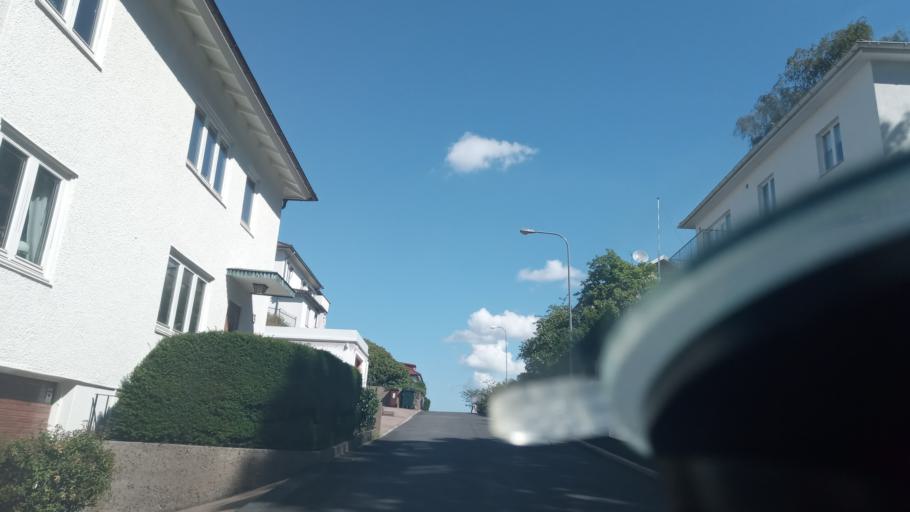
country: SE
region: Vaestra Goetaland
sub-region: Molndal
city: Moelndal
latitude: 57.6929
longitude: 12.0099
